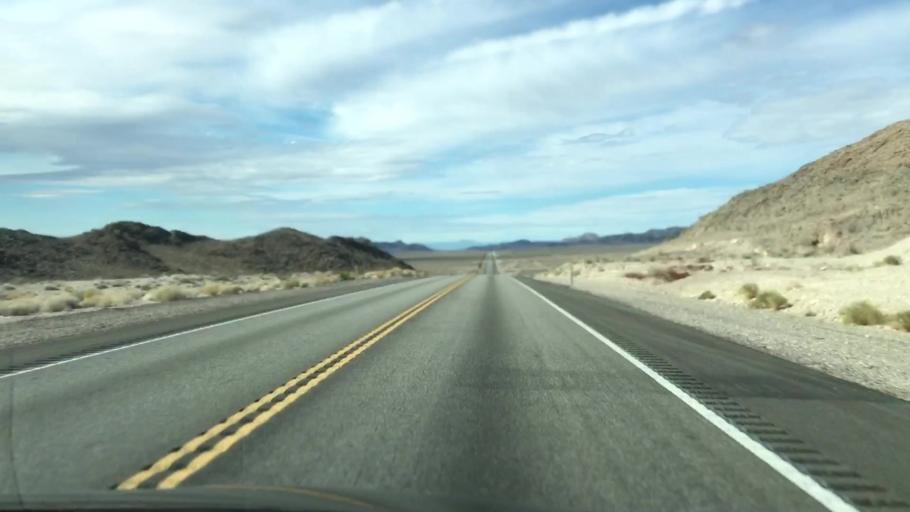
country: US
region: Nevada
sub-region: Nye County
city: Pahrump
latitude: 36.5812
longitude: -116.2032
